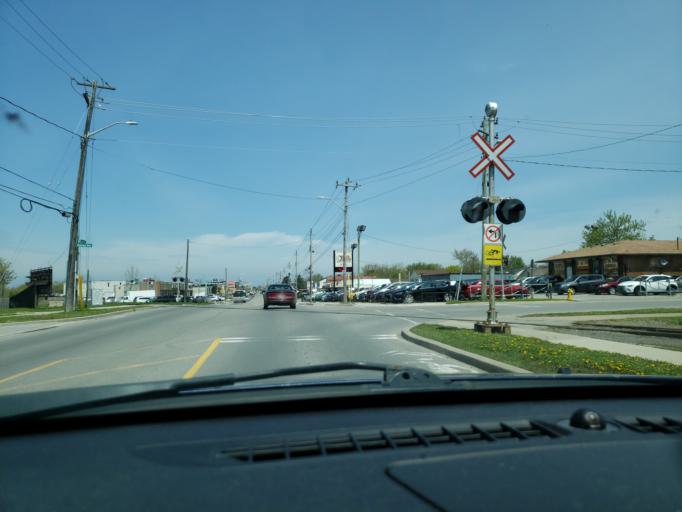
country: CA
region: Ontario
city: Thorold
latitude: 43.1438
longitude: -79.2141
